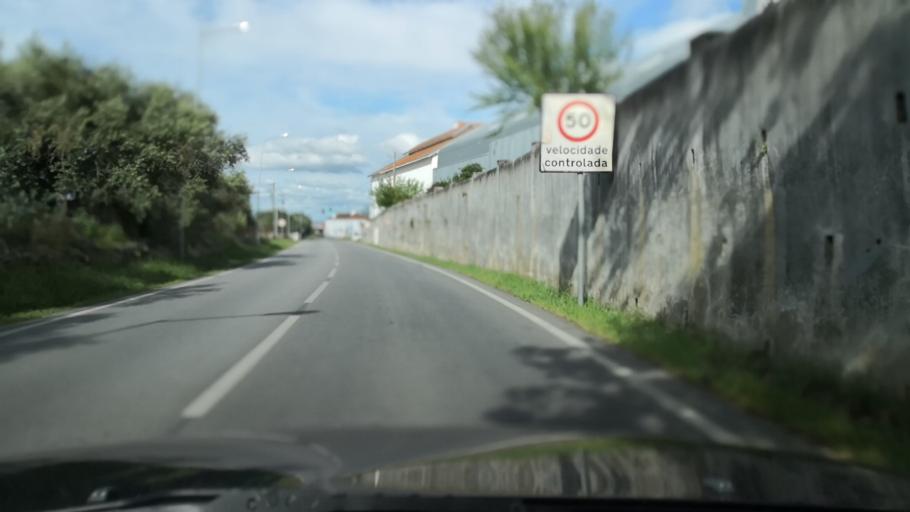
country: PT
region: Evora
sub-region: Evora
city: Evora
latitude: 38.5788
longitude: -7.9067
